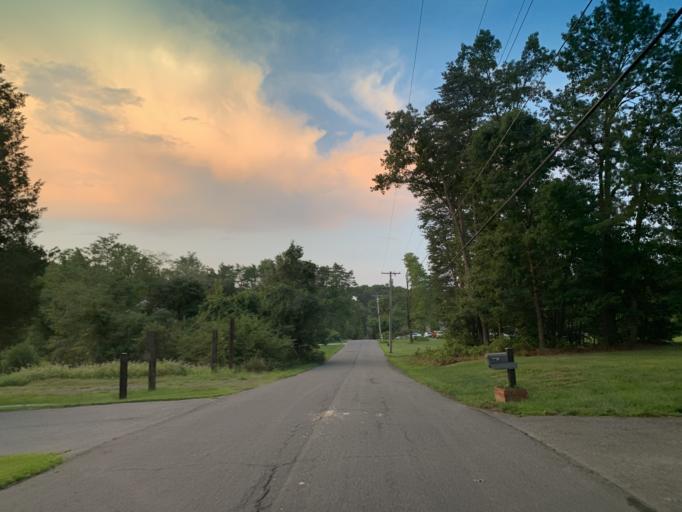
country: US
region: Maryland
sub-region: Harford County
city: Edgewood
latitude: 39.4173
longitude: -76.3373
